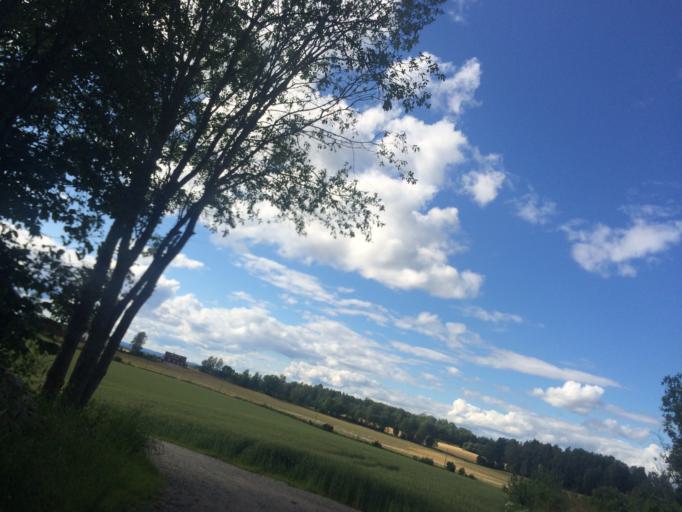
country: NO
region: Akershus
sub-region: As
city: As
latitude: 59.6749
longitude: 10.7860
